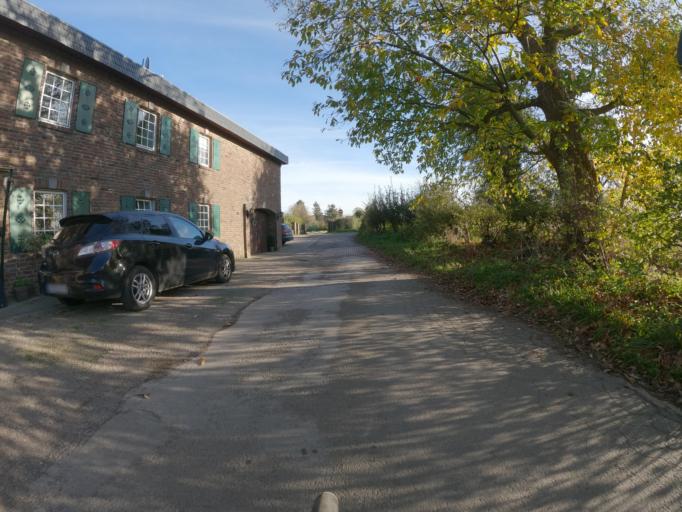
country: DE
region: North Rhine-Westphalia
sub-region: Regierungsbezirk Koln
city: Aachen
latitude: 50.8188
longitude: 6.0874
